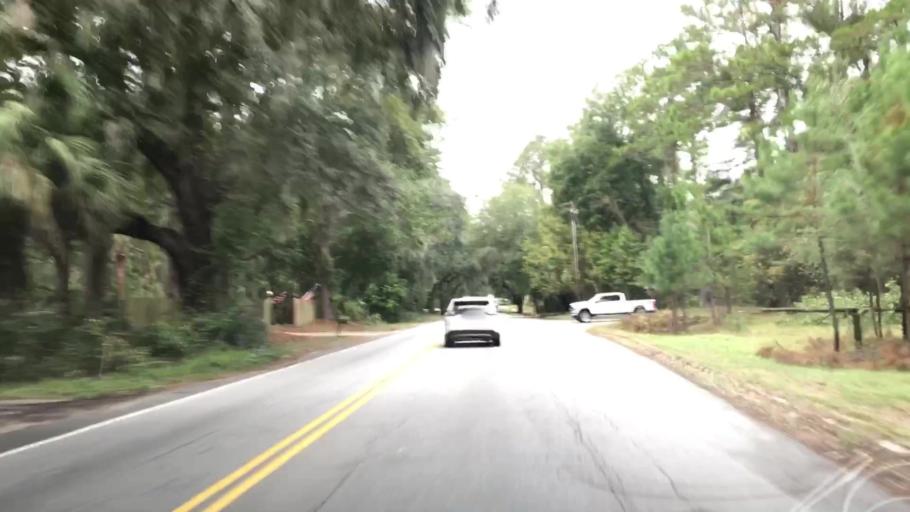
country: US
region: South Carolina
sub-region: Beaufort County
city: Bluffton
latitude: 32.2402
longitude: -80.8840
